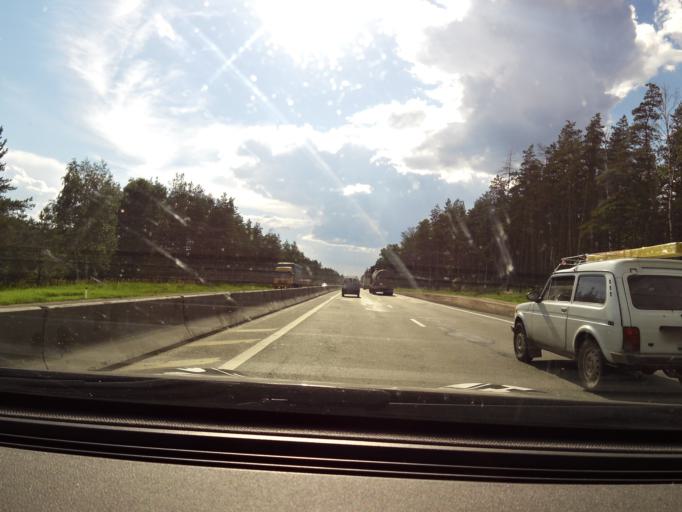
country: RU
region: Nizjnij Novgorod
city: Pyra
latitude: 56.2953
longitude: 43.4020
